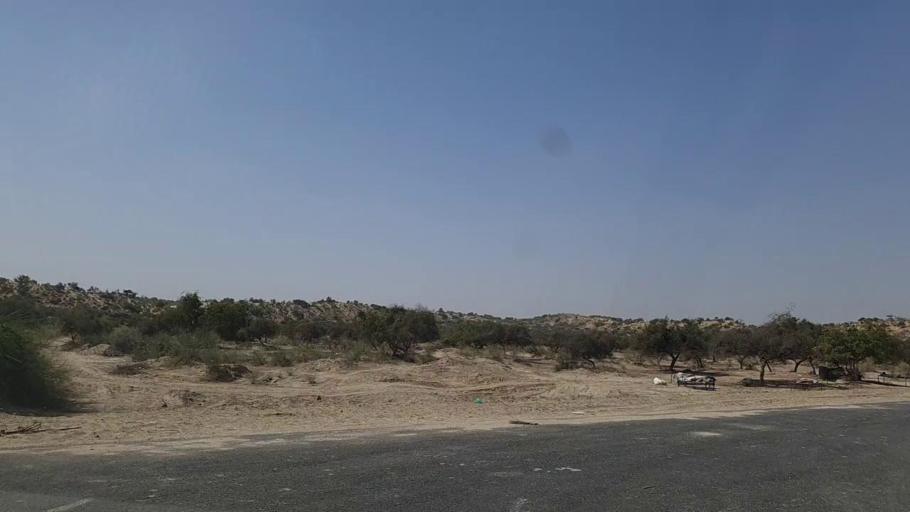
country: PK
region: Sindh
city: Diplo
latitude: 24.5860
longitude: 69.5611
